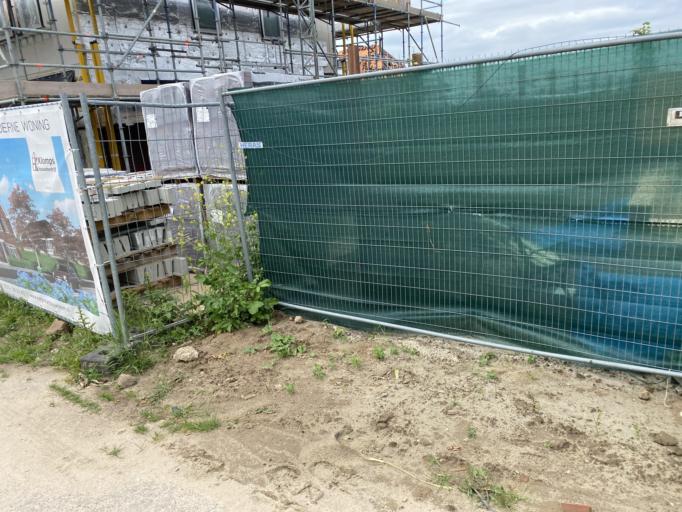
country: NL
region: Gelderland
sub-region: Gemeente Westervoort
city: Westervoort
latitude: 51.9310
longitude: 5.9852
